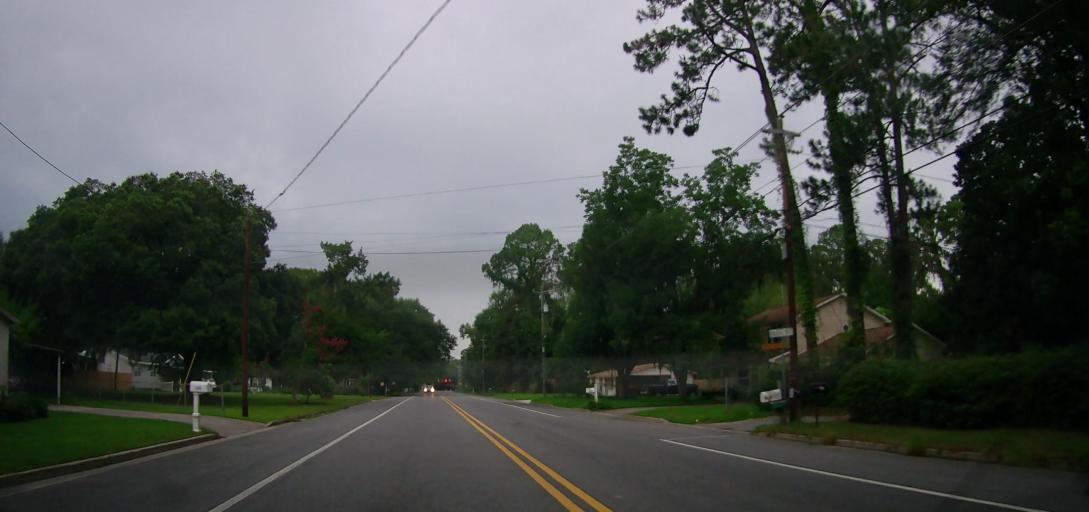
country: US
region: Georgia
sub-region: Glynn County
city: Dock Junction
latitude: 31.2097
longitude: -81.4989
